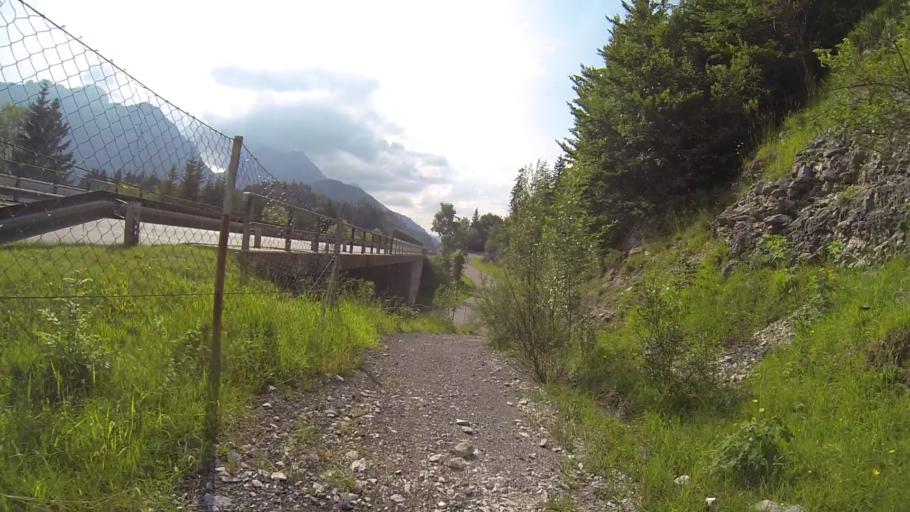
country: AT
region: Tyrol
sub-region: Politischer Bezirk Reutte
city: Pflach
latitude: 47.5221
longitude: 10.7134
